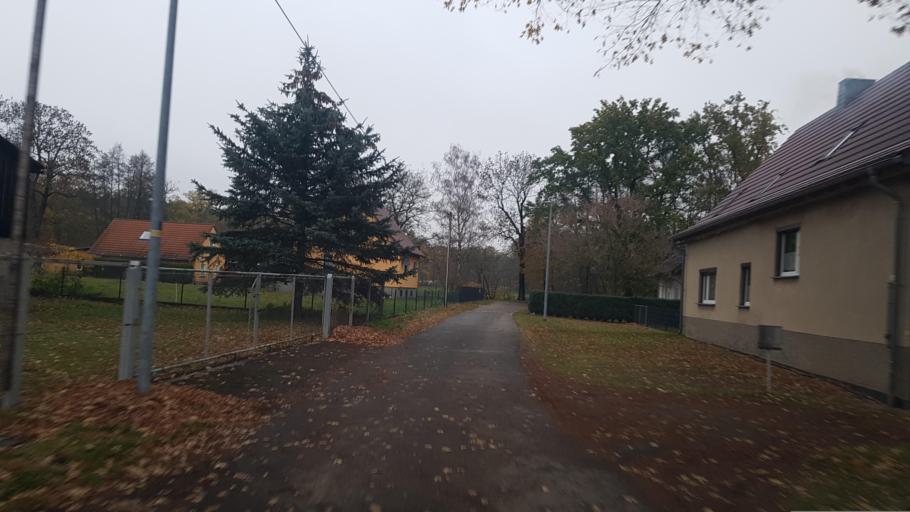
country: DE
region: Brandenburg
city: Hermsdorf
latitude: 51.4029
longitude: 13.9002
